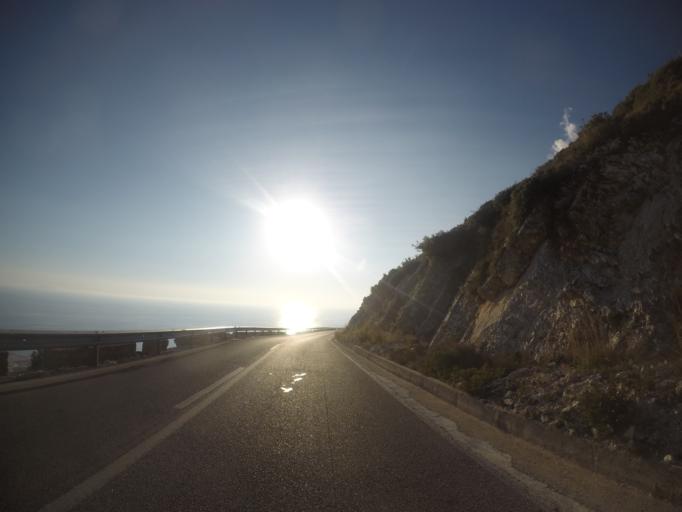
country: AL
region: Vlore
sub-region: Rrethi i Vlores
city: Vranisht
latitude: 40.1796
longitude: 19.6010
